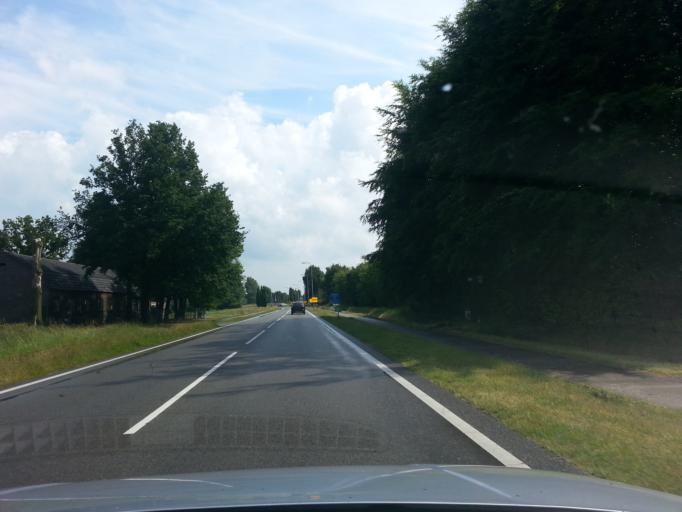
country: NL
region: Limburg
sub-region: Gemeente Venray
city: Venray
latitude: 51.5000
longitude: 5.8906
